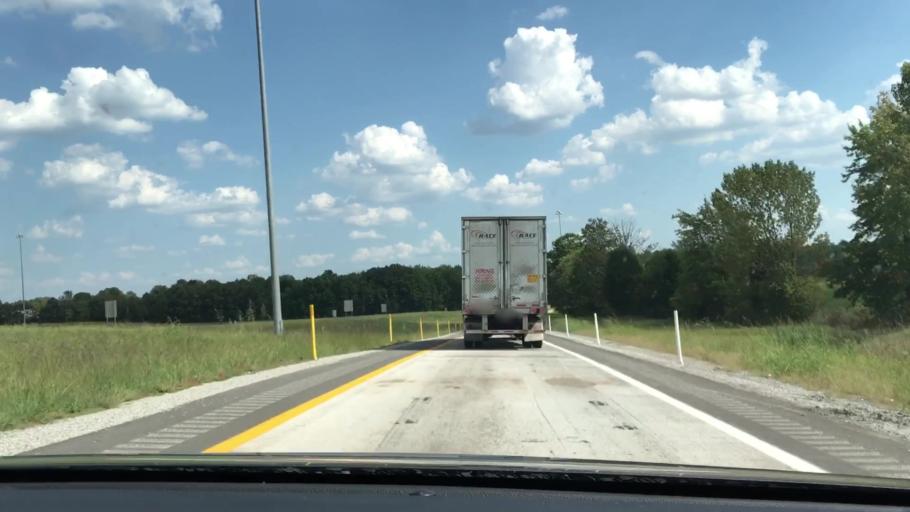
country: US
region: Kentucky
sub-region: Ohio County
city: Beaver Dam
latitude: 37.3824
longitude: -86.8112
